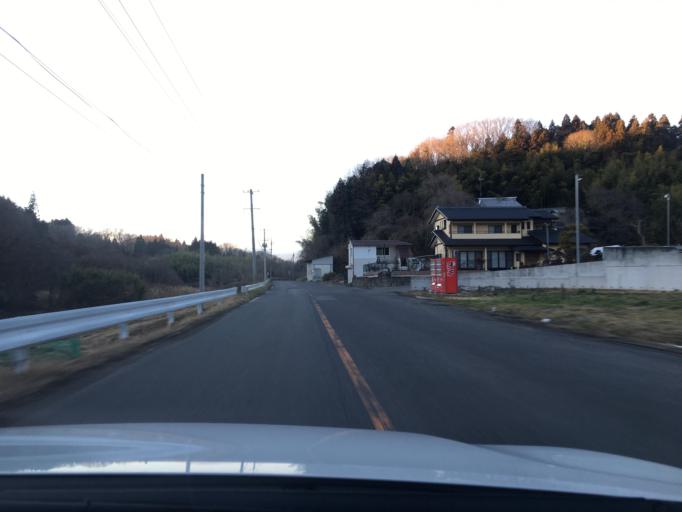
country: JP
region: Fukushima
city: Miharu
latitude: 37.4499
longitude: 140.5093
